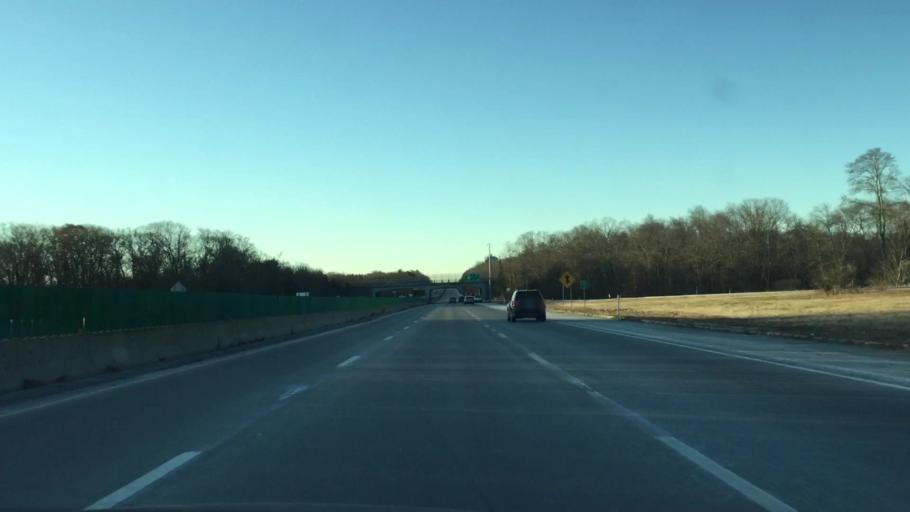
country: US
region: Massachusetts
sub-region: Norfolk County
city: Avon
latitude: 42.0966
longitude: -71.0587
